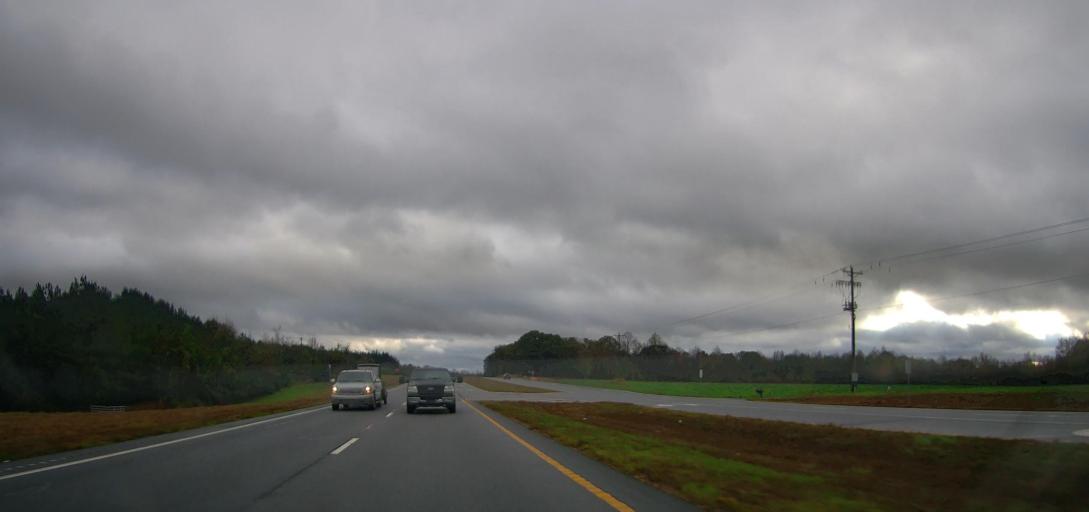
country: US
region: Georgia
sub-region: Banks County
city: Homer
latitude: 34.3984
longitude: -83.4871
